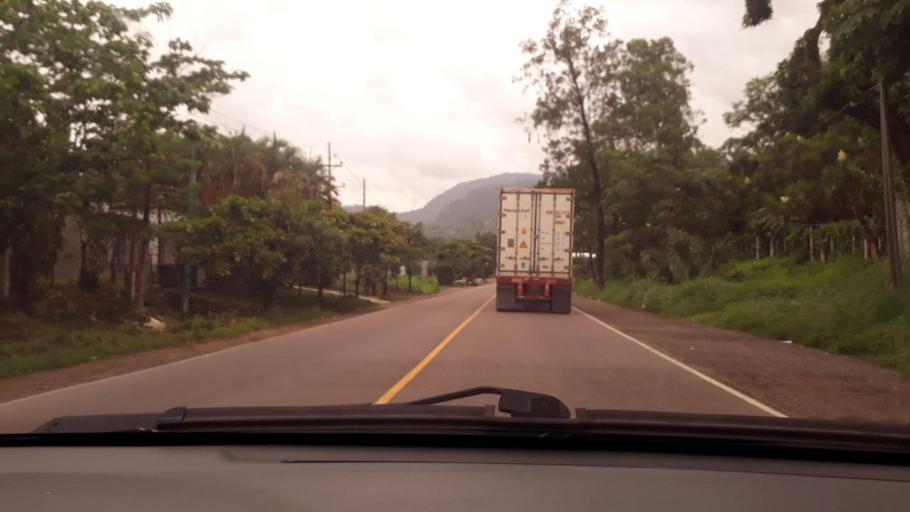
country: GT
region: Chiquimula
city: Quezaltepeque
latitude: 14.6250
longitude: -89.4450
